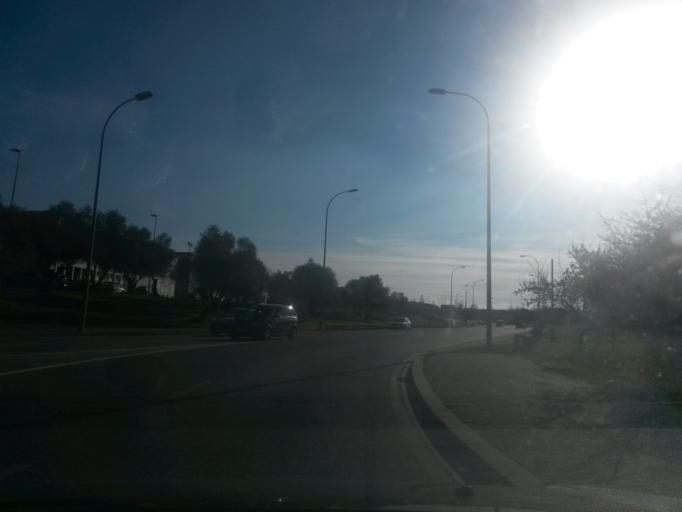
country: ES
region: Catalonia
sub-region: Provincia de Girona
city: Salt
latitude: 41.9604
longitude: 2.8103
